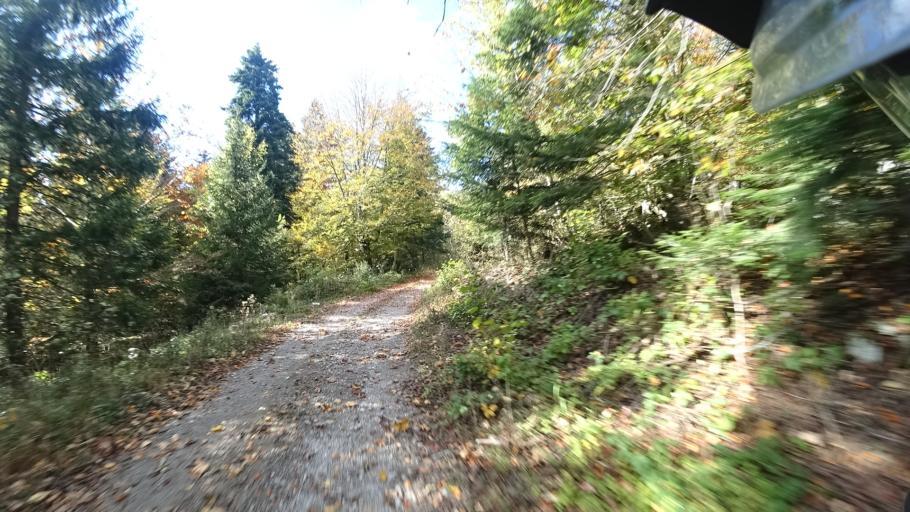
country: HR
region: Karlovacka
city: Plaski
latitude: 45.0685
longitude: 15.3350
